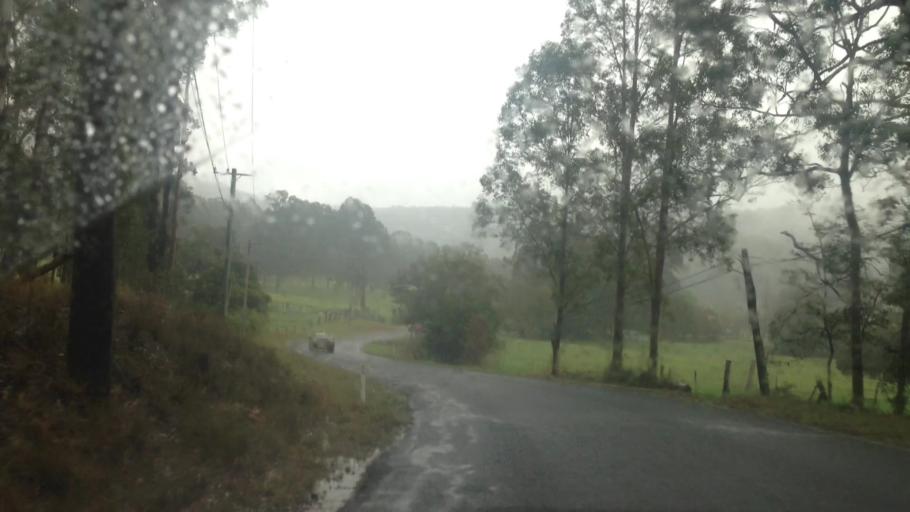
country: AU
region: New South Wales
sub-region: Wyong Shire
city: Little Jilliby
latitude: -33.2069
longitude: 151.3668
